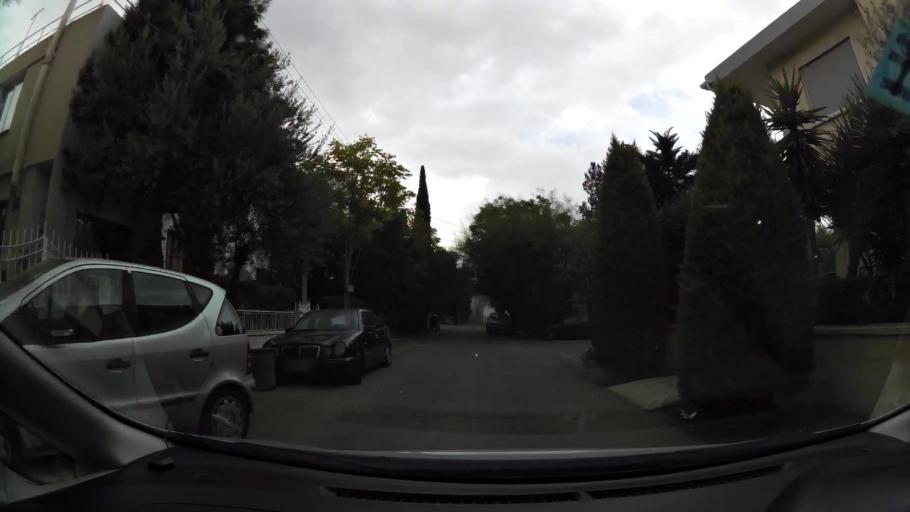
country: CY
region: Lefkosia
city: Nicosia
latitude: 35.1566
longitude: 33.3529
